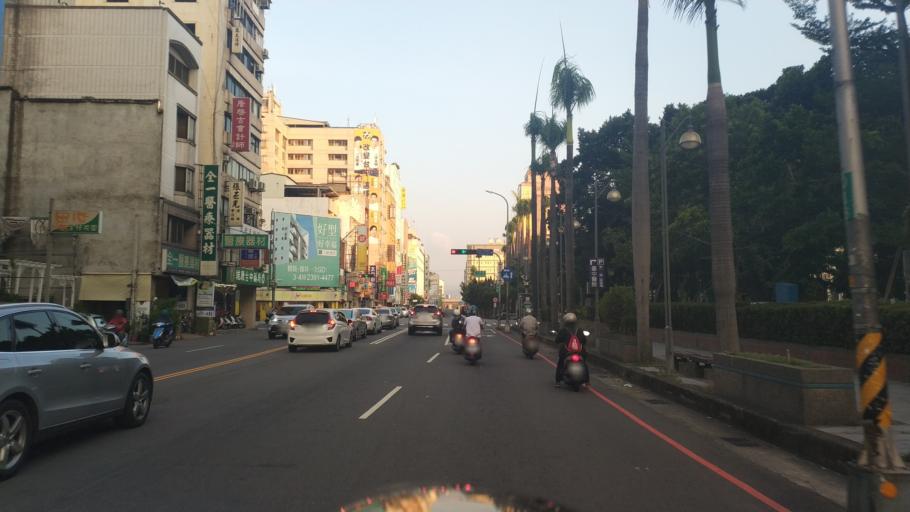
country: TW
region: Taiwan
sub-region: Taichung City
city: Taichung
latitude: 24.1406
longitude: 120.6767
